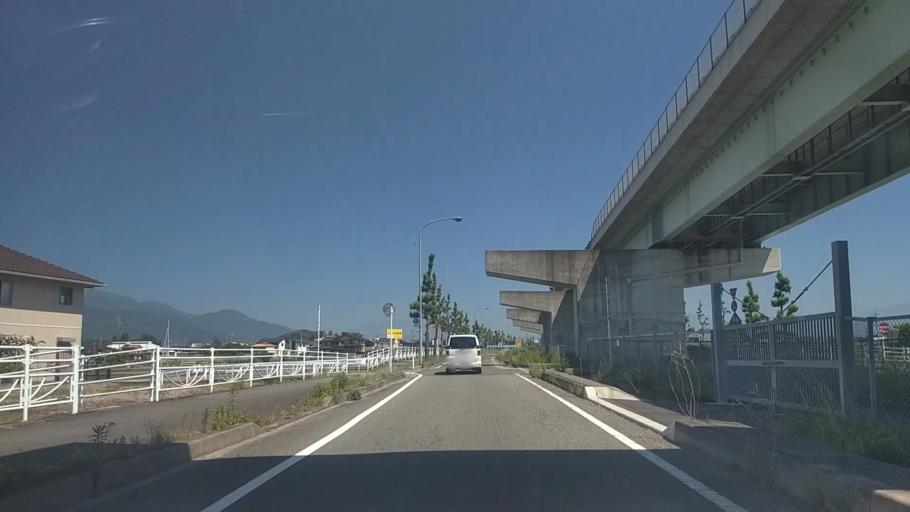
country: JP
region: Yamanashi
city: Ryuo
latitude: 35.5843
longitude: 138.4746
